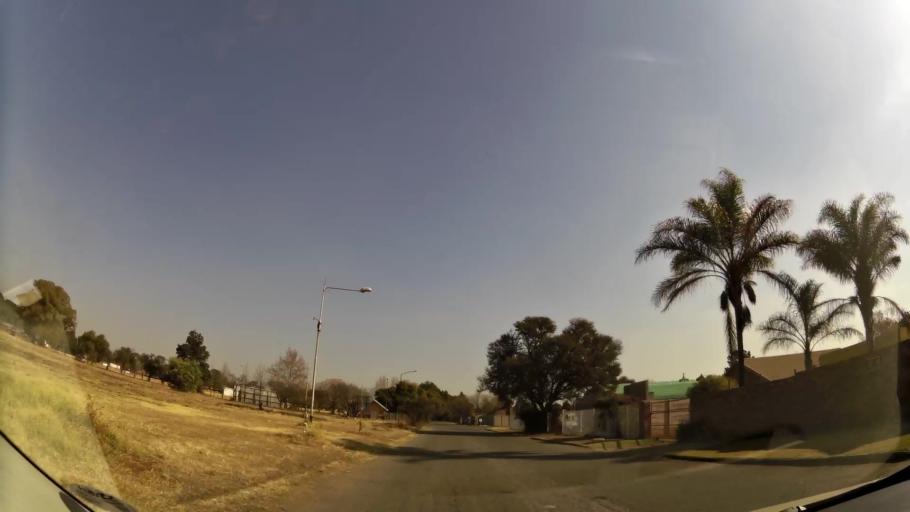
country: ZA
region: Gauteng
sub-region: West Rand District Municipality
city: Randfontein
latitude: -26.1597
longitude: 27.7045
